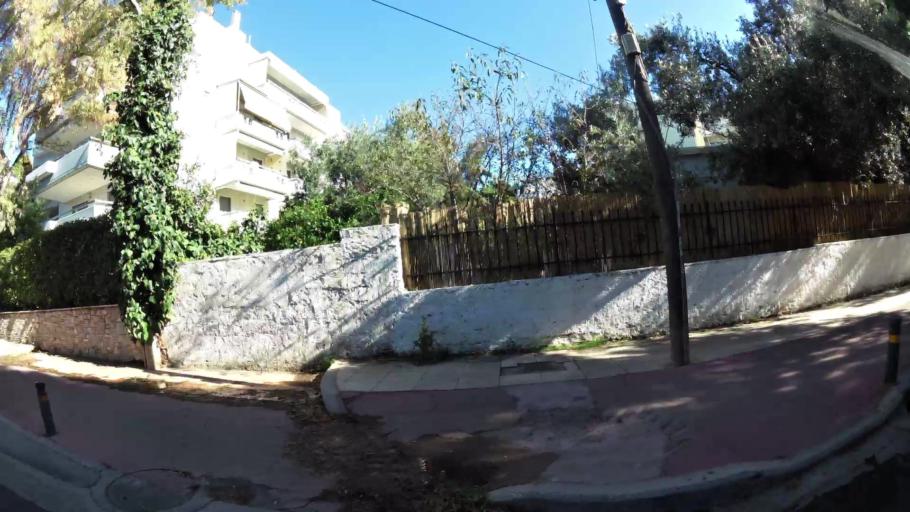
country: GR
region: Attica
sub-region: Nomarchia Athinas
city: Vrilissia
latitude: 38.0319
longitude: 23.8354
